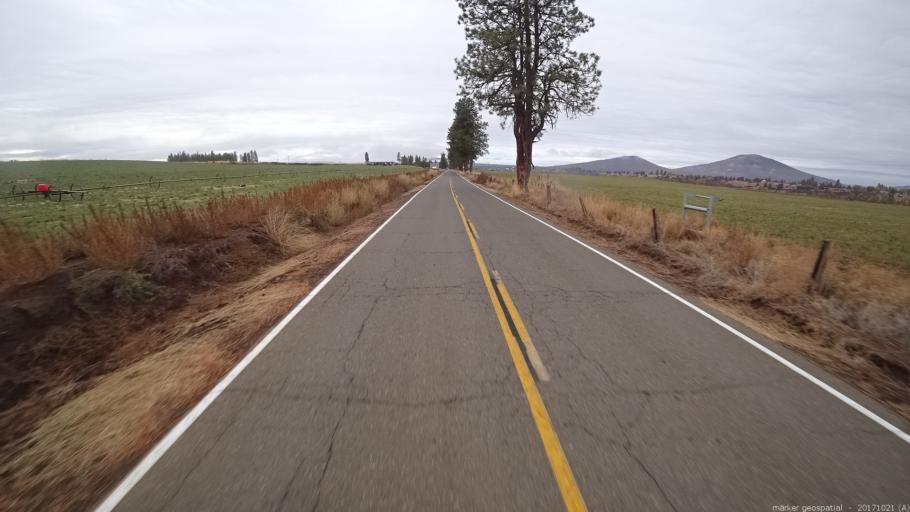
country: US
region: California
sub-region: Shasta County
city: Burney
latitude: 41.0237
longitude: -121.4062
